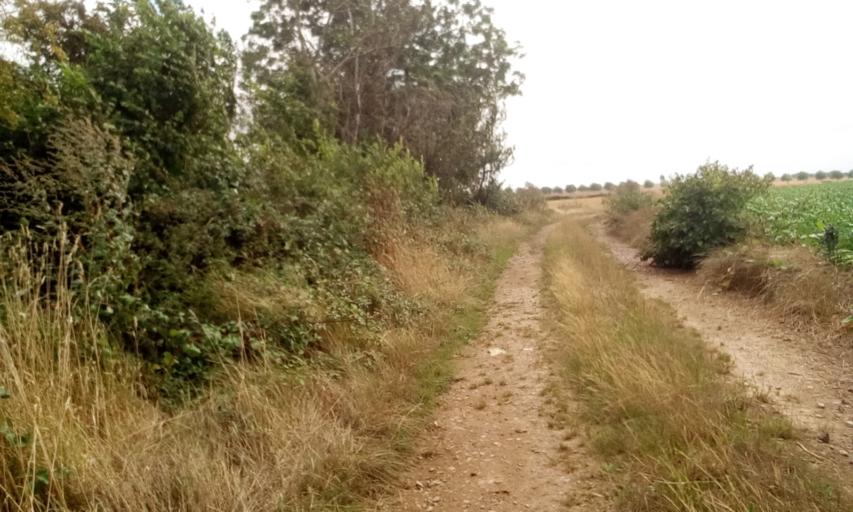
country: FR
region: Lower Normandy
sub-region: Departement du Calvados
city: Cheux
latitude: 49.1816
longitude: -0.5432
